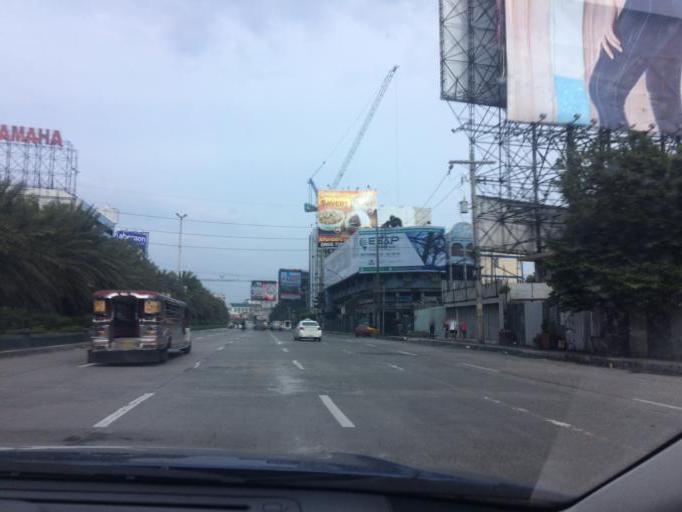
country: PH
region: Metro Manila
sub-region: Makati City
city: Makati City
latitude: 14.5377
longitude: 120.9989
